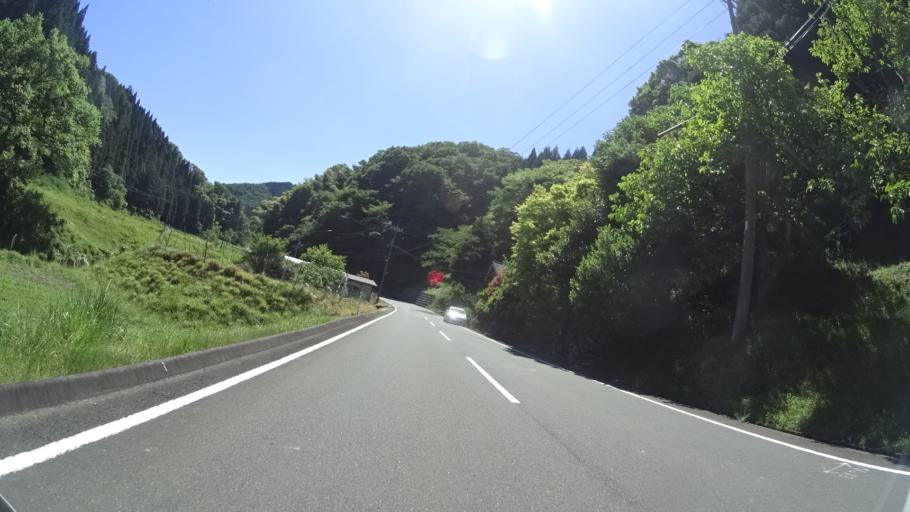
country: JP
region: Kyoto
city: Fukuchiyama
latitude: 35.4157
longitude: 135.0626
